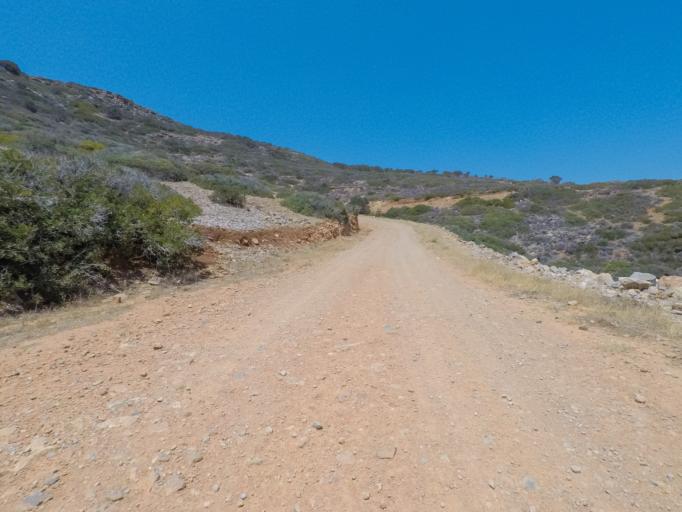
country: GR
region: Crete
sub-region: Nomos Lasithiou
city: Elounda
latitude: 35.3226
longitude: 25.7585
